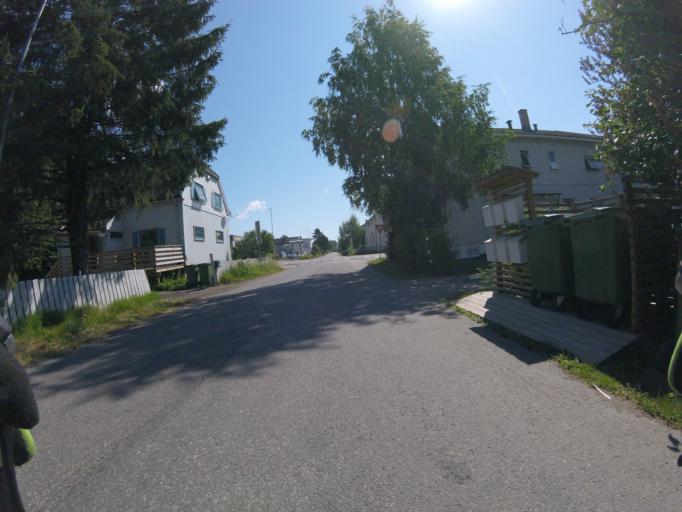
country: NO
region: Akershus
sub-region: Skedsmo
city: Lillestrom
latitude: 59.9612
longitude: 11.0496
